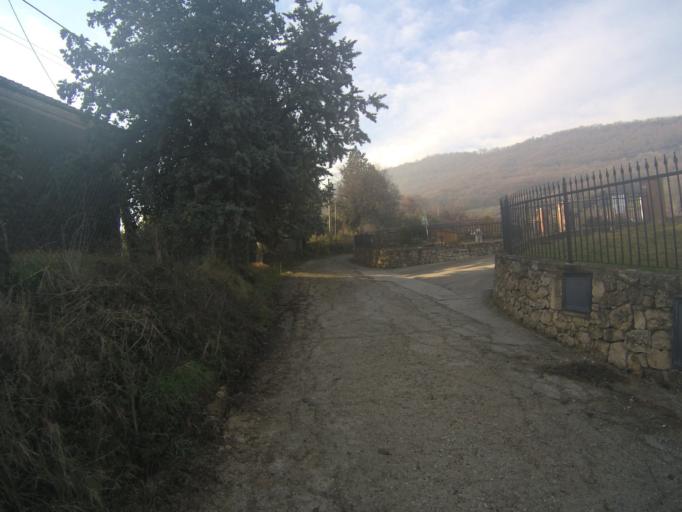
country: IT
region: Veneto
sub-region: Provincia di Vicenza
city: Lumignano
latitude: 45.4448
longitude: 11.5819
